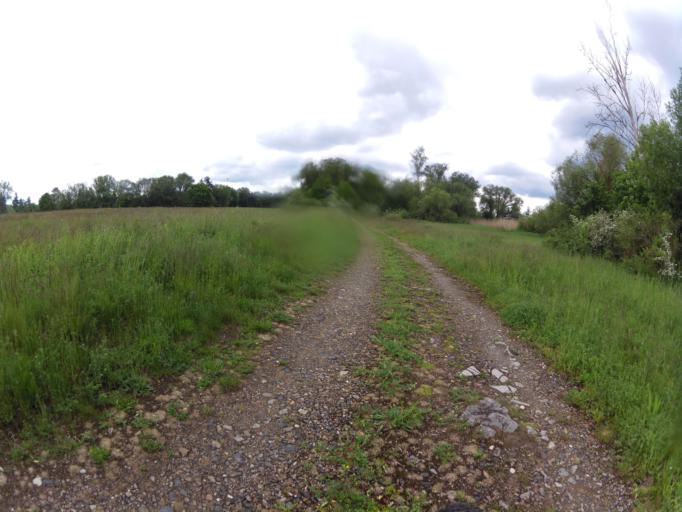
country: DE
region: Bavaria
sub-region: Regierungsbezirk Unterfranken
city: Sommerach
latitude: 49.8156
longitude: 10.2179
